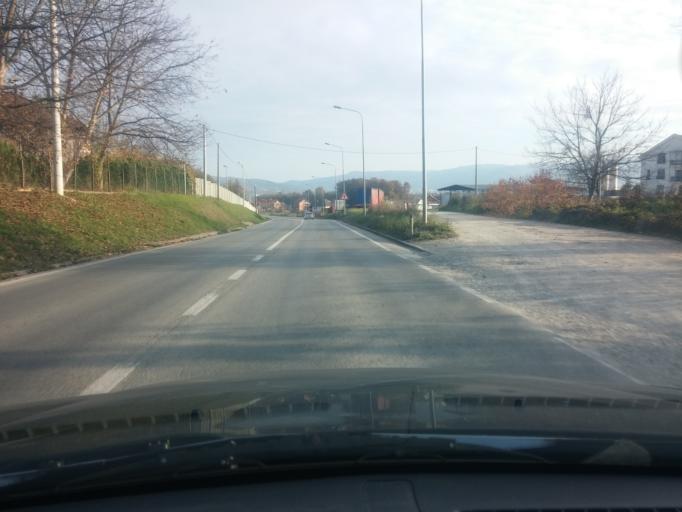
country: BA
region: Republika Srpska
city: Banja Luka
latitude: 44.8246
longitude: 17.1925
